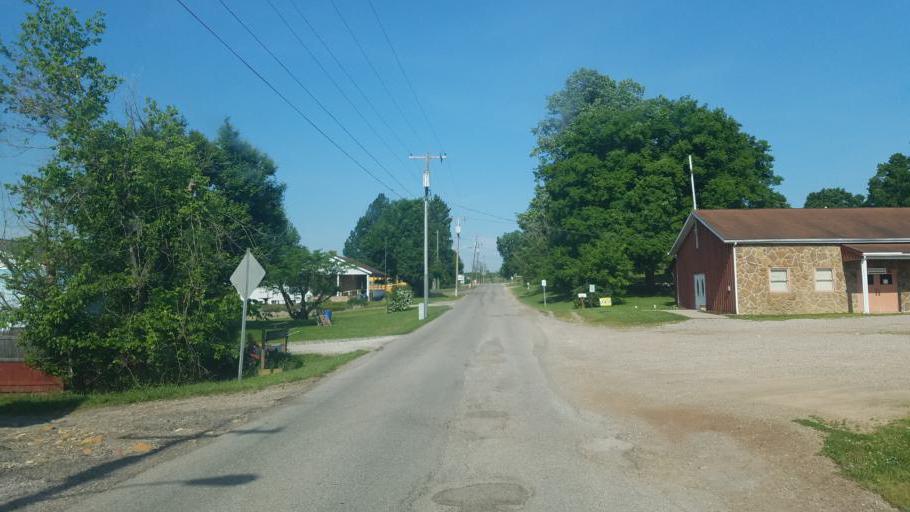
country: US
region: Ohio
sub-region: Gallia County
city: Gallipolis
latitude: 38.9764
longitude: -82.3475
